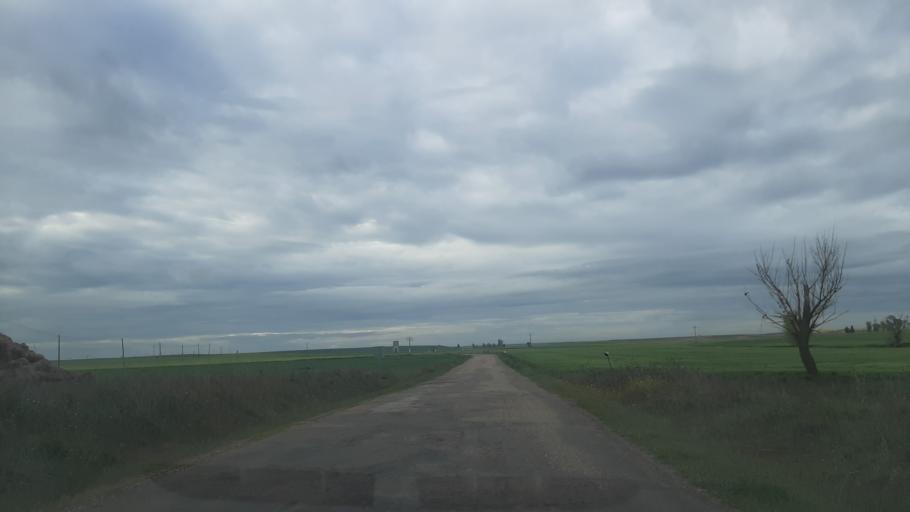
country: ES
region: Castille and Leon
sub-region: Provincia de Salamanca
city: Villaflores
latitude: 41.0804
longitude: -5.2199
